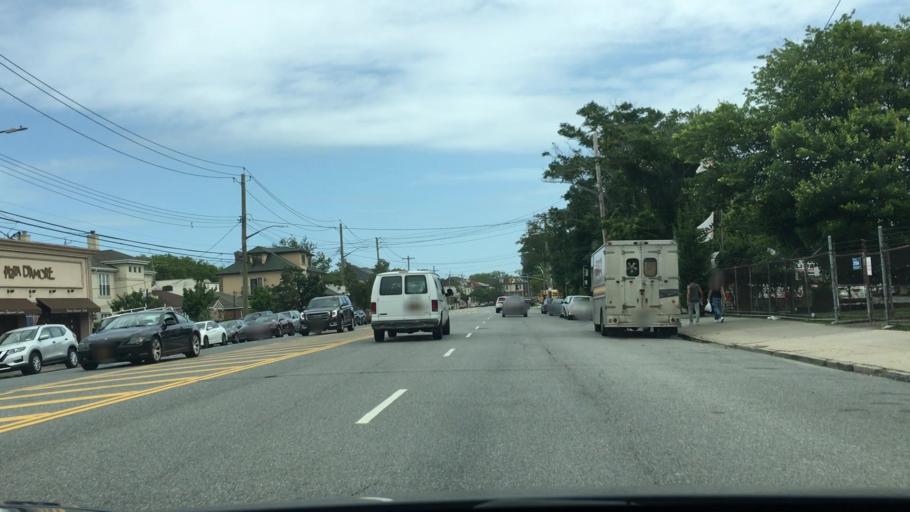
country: US
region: New York
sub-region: Kings County
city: Brooklyn
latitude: 40.6148
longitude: -73.9132
